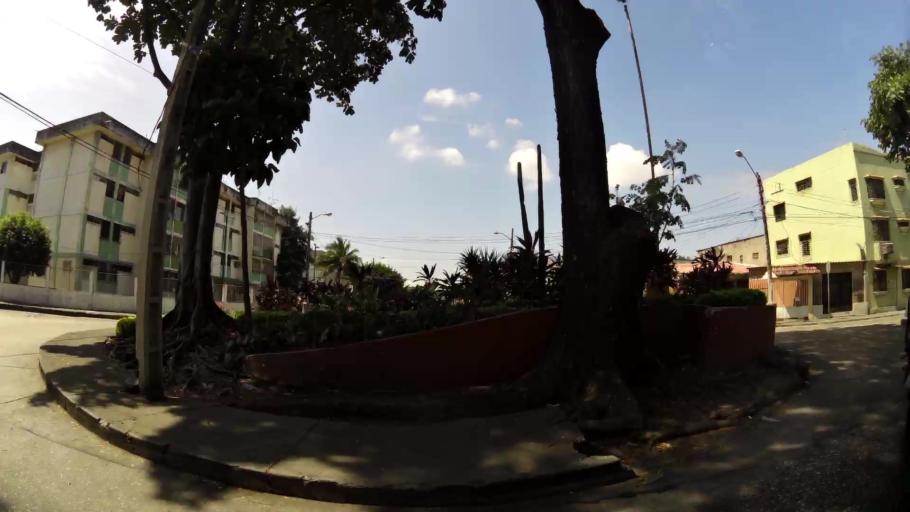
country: EC
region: Guayas
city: Guayaquil
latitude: -2.2339
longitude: -79.9037
